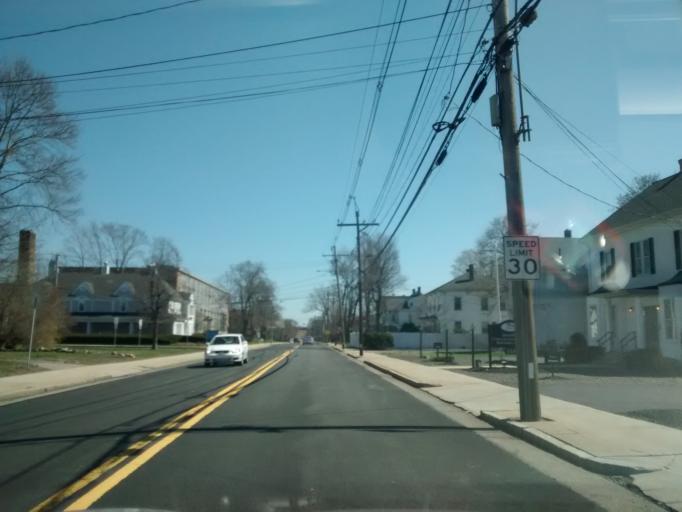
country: US
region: Massachusetts
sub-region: Middlesex County
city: Framingham
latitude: 42.2874
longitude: -71.4234
